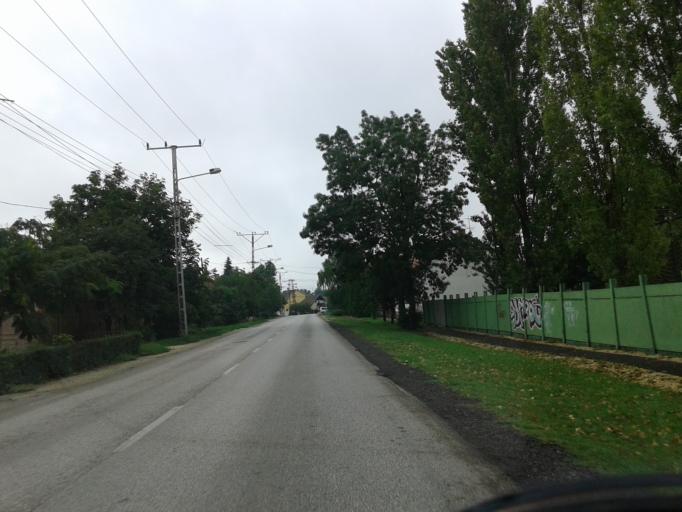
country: HU
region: Csongrad
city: Szeged
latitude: 46.2568
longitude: 20.1919
